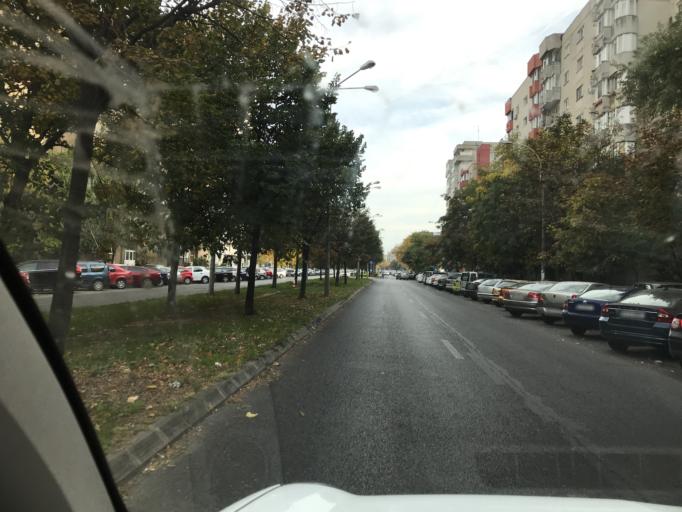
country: RO
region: Bucuresti
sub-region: Municipiul Bucuresti
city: Bucuresti
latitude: 44.4226
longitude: 26.0640
